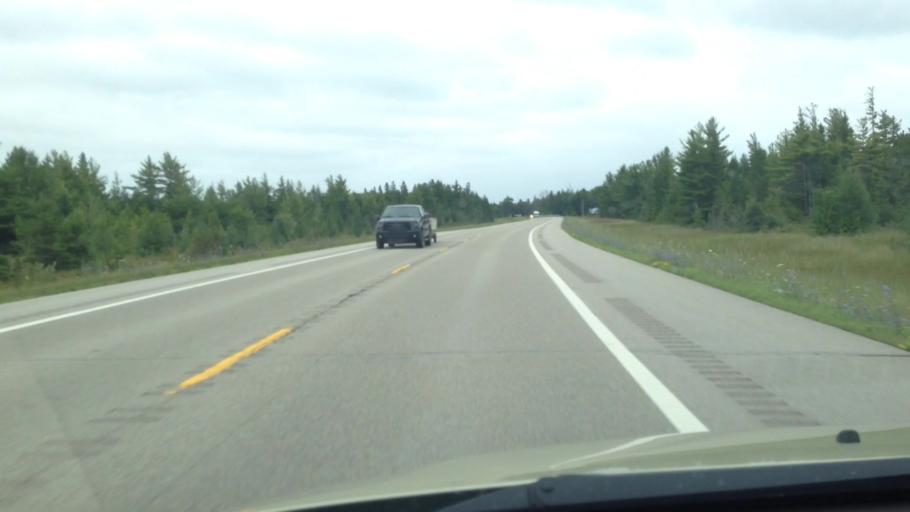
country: US
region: Michigan
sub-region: Mackinac County
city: Saint Ignace
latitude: 45.9208
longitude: -84.8766
